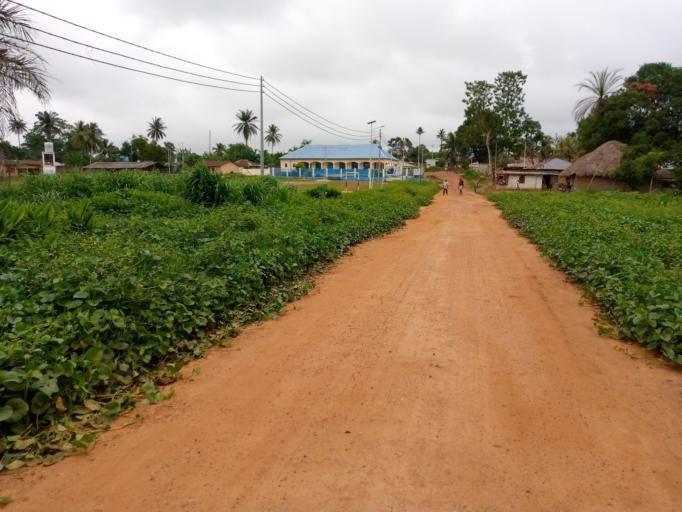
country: SL
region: Southern Province
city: Sumbuya
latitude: 7.5652
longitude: -12.0898
